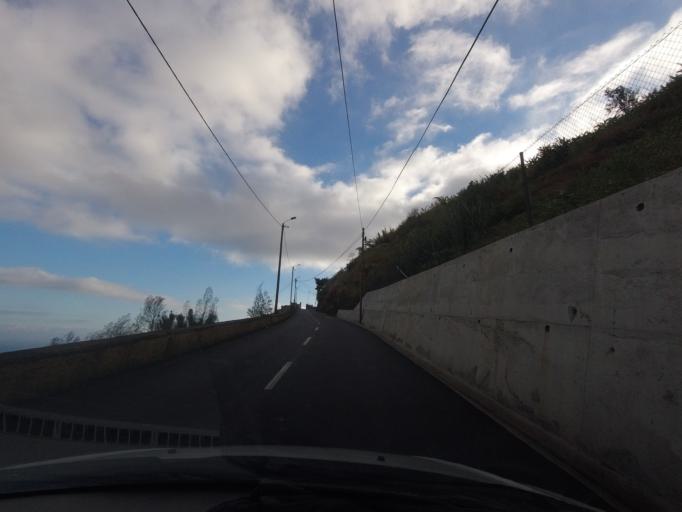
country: PT
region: Madeira
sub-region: Funchal
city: Nossa Senhora do Monte
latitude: 32.6714
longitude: -16.9193
